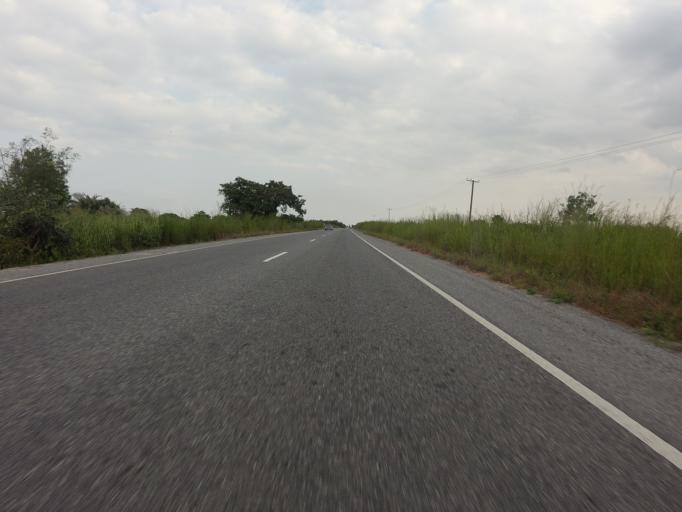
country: GH
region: Volta
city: Ho
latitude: 6.2425
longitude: 0.5510
